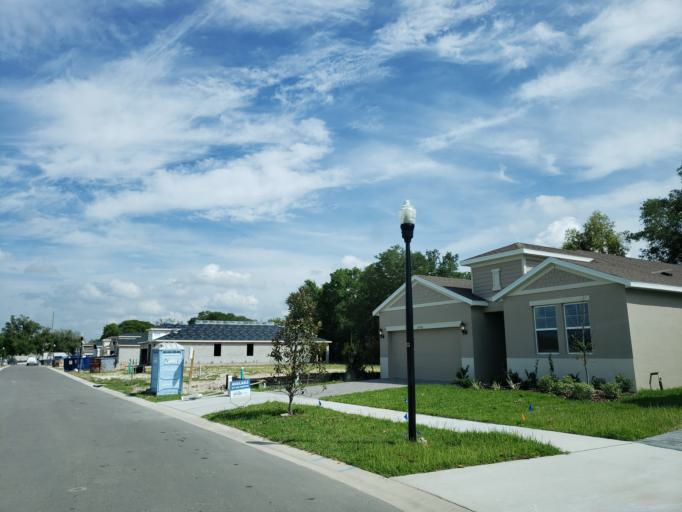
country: US
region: Florida
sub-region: Hillsborough County
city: Riverview
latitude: 27.8978
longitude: -82.3214
